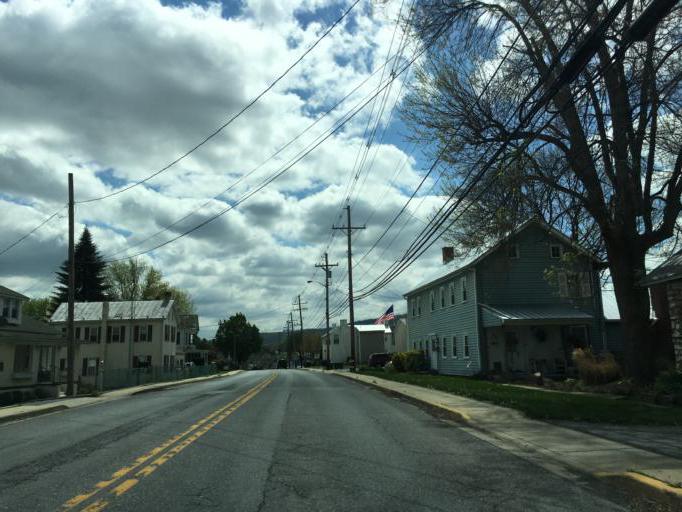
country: US
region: Maryland
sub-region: Frederick County
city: Thurmont
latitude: 39.6204
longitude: -77.4137
